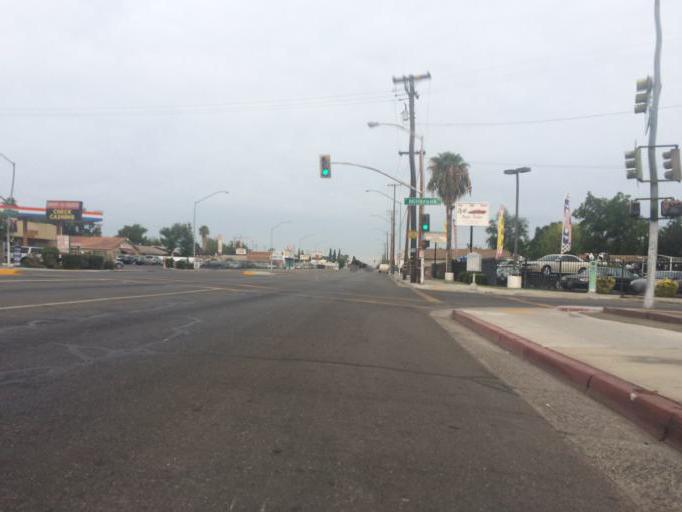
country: US
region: California
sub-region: Fresno County
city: Fresno
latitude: 36.7506
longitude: -119.7638
